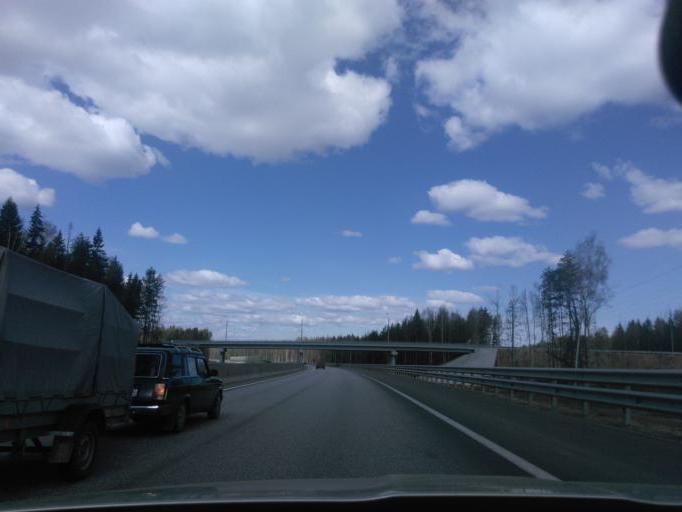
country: RU
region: Moskovskaya
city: Peshki
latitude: 56.1381
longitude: 37.0973
